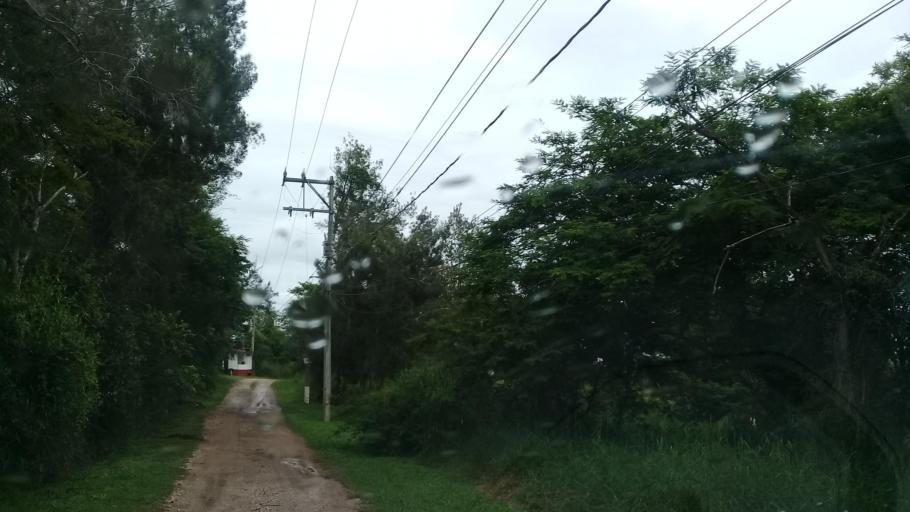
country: MX
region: Veracruz
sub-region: Emiliano Zapata
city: Jacarandas
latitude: 19.5086
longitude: -96.8403
